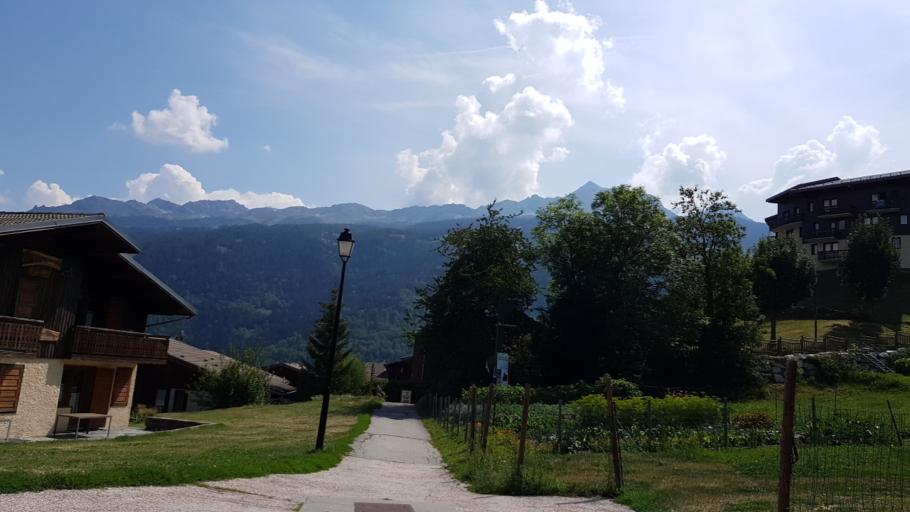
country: FR
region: Rhone-Alpes
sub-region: Departement de la Savoie
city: Belle-Plagne
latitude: 45.5601
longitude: 6.7374
